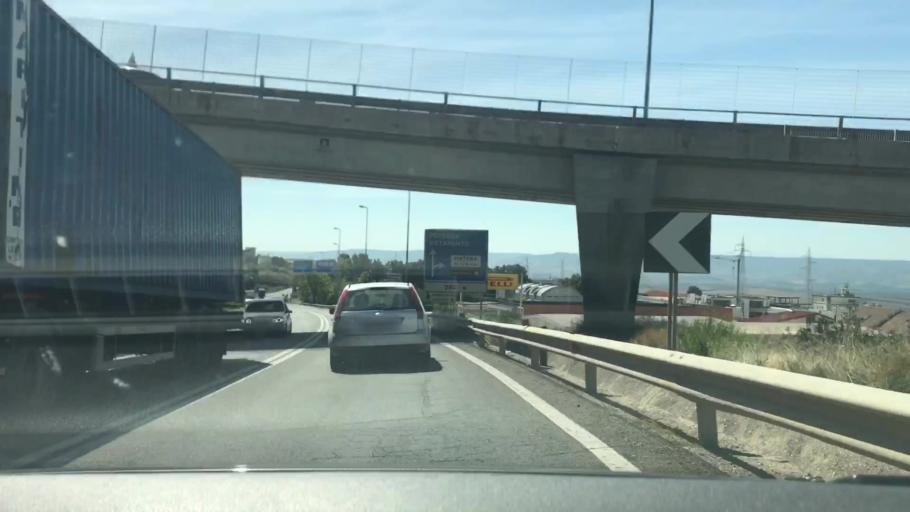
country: IT
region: Basilicate
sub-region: Provincia di Matera
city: Matera
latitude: 40.6731
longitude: 16.5775
